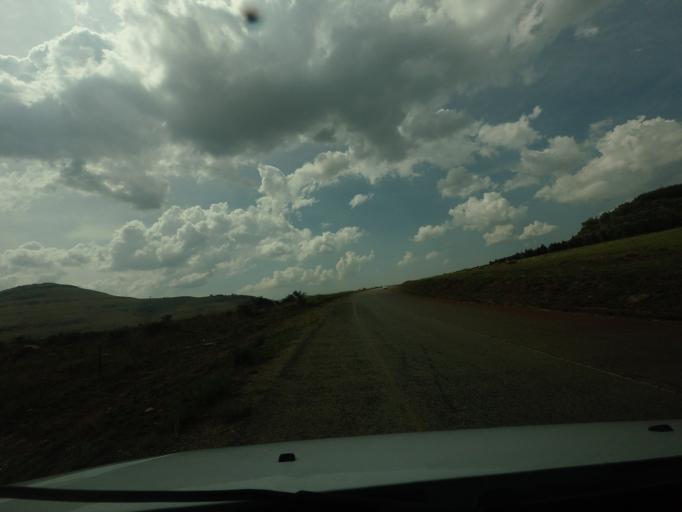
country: ZA
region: Mpumalanga
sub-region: Ehlanzeni District
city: Graksop
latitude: -24.7091
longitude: 30.8180
